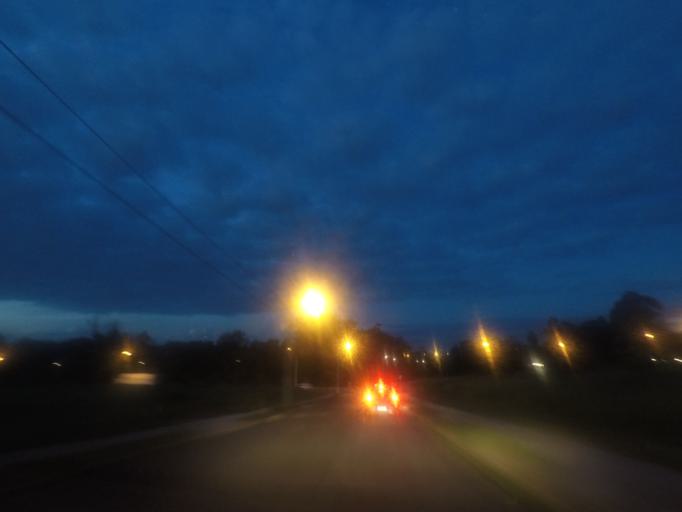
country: BR
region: Parana
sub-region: Pinhais
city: Pinhais
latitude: -25.3837
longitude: -49.2053
